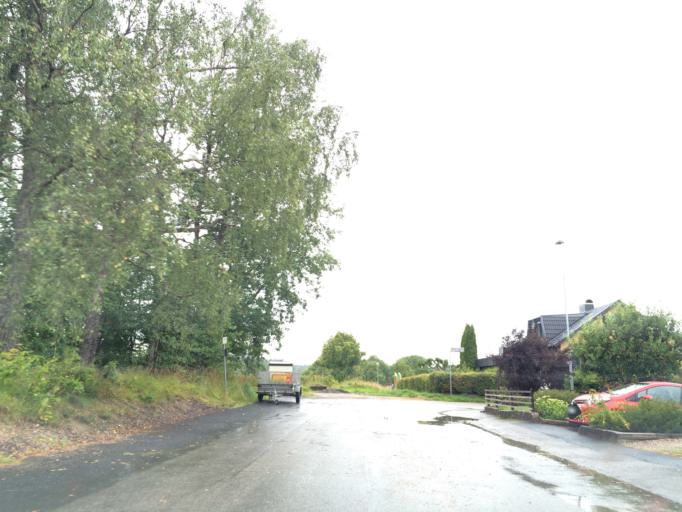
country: SE
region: Vaestra Goetaland
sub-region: Trollhattan
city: Trollhattan
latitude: 58.2794
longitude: 12.2564
